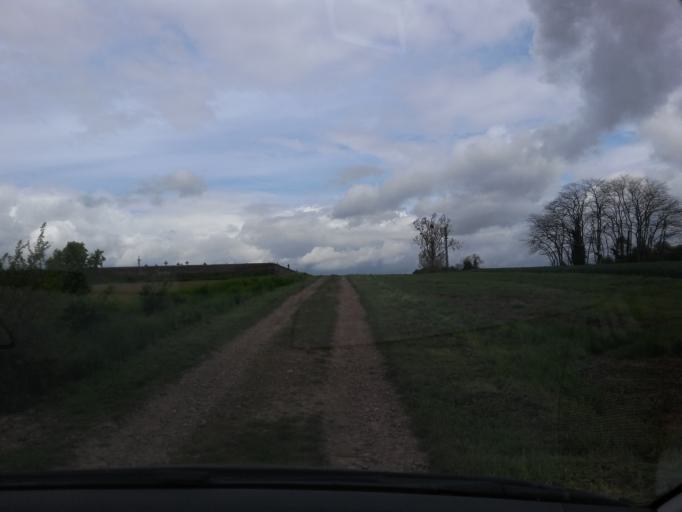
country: FR
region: Picardie
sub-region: Departement de l'Oise
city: Grandfresnoy
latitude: 49.3687
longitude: 2.6621
